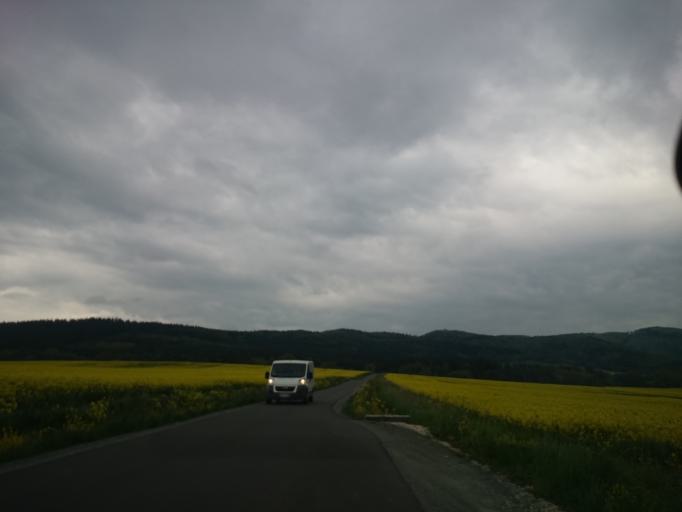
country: PL
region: Lower Silesian Voivodeship
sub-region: Powiat klodzki
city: Klodzko
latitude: 50.4245
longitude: 16.7149
